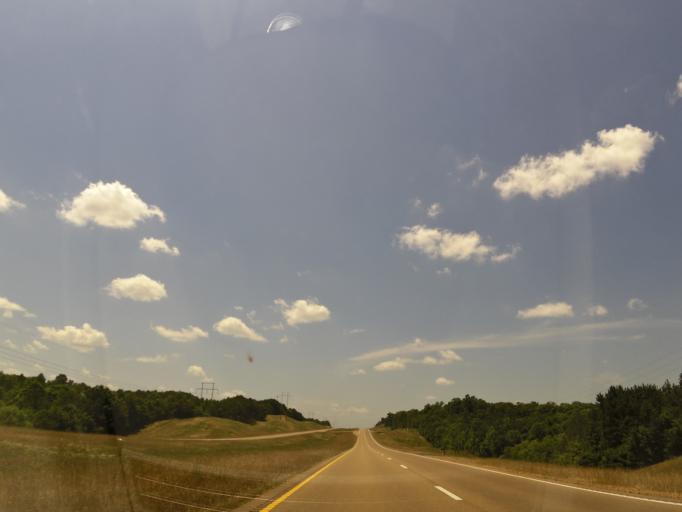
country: US
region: Mississippi
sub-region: Lafayette County
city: Oxford
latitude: 34.3200
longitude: -89.3671
